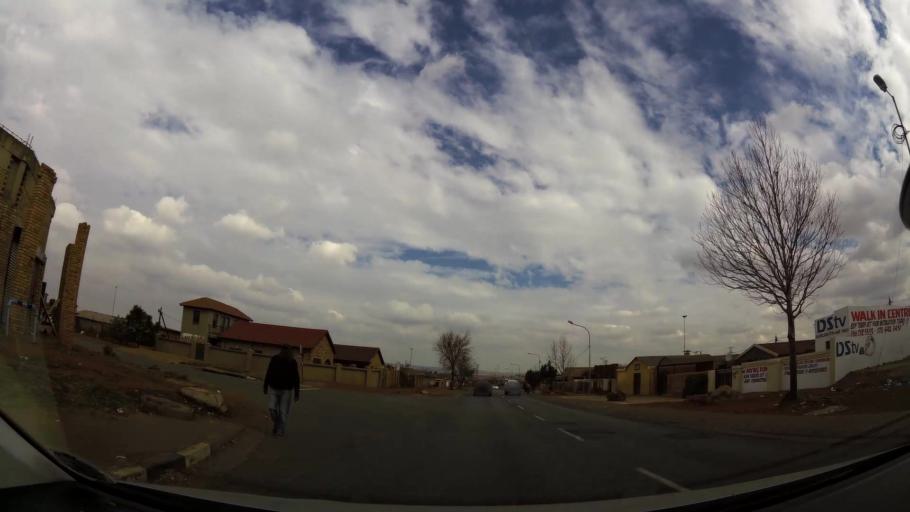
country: ZA
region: Gauteng
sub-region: City of Johannesburg Metropolitan Municipality
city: Soweto
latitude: -26.2743
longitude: 27.8463
